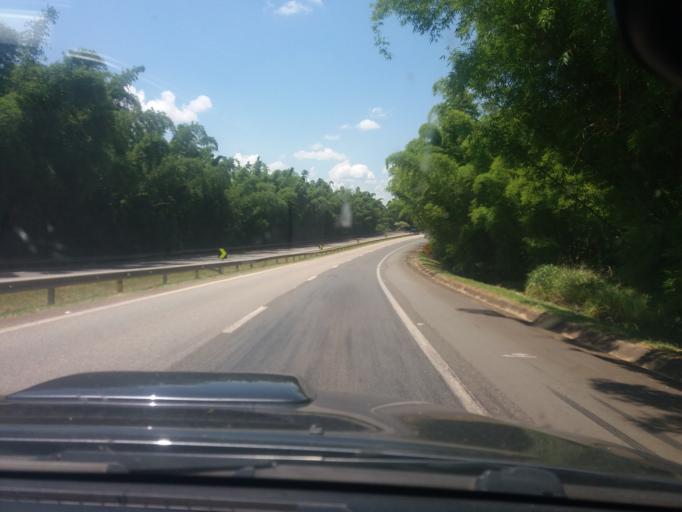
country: BR
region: Sao Paulo
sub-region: Tatui
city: Tatui
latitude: -23.4067
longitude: -47.9233
